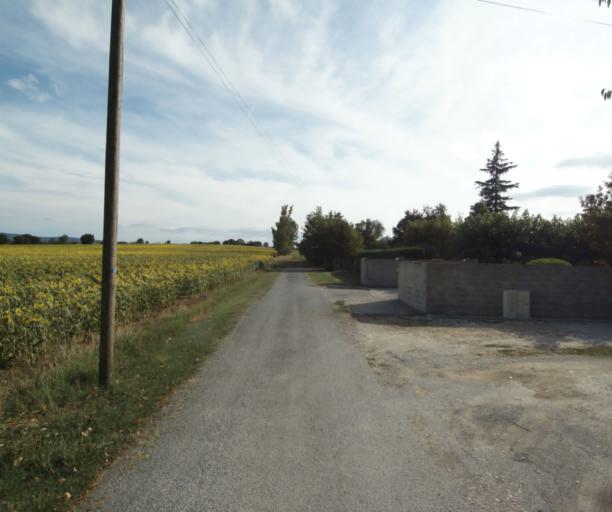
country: FR
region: Midi-Pyrenees
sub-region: Departement du Tarn
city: Puylaurens
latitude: 43.5165
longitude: 1.9984
